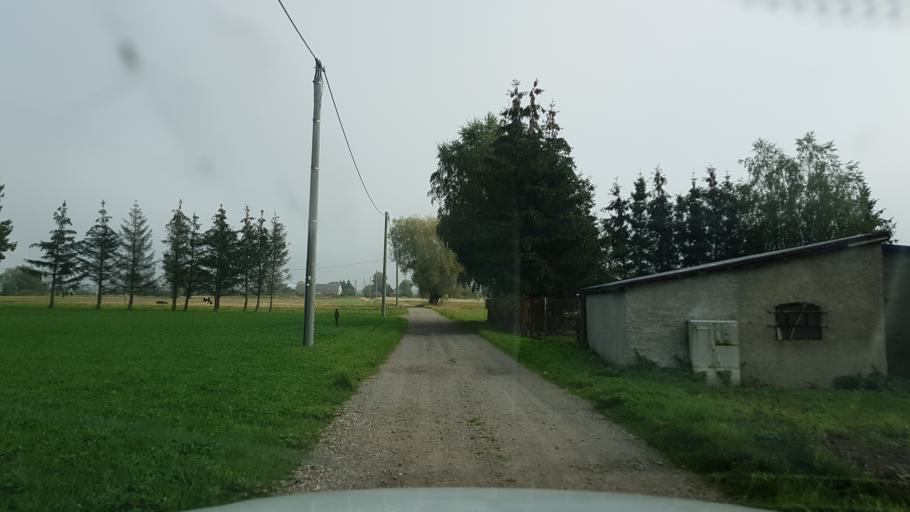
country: PL
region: West Pomeranian Voivodeship
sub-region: Powiat koszalinski
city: Mielno
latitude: 54.2304
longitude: 15.9507
